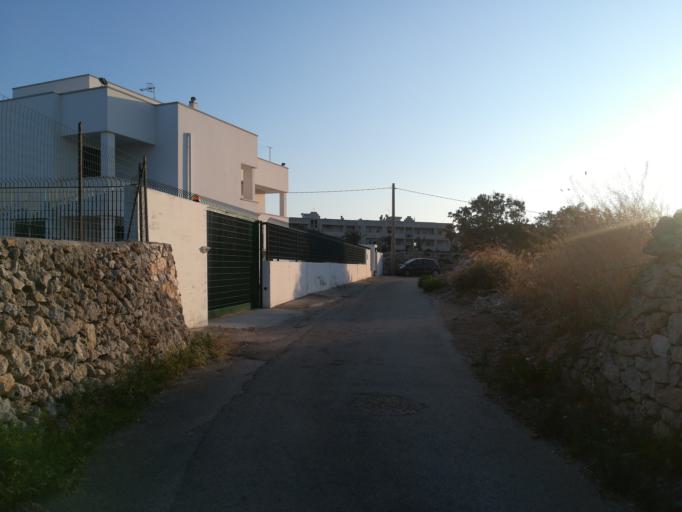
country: IT
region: Apulia
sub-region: Provincia di Bari
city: Polignano a Mare
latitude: 40.9898
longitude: 17.2318
